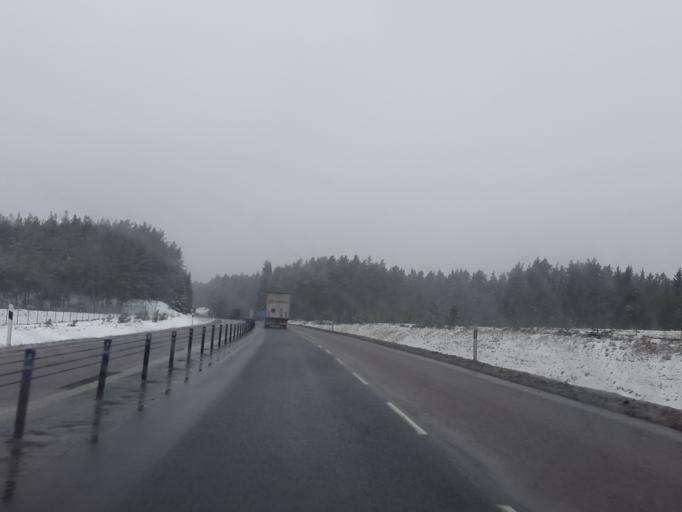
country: SE
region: Joenkoeping
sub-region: Jonkopings Kommun
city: Jonkoping
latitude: 57.7735
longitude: 14.0764
